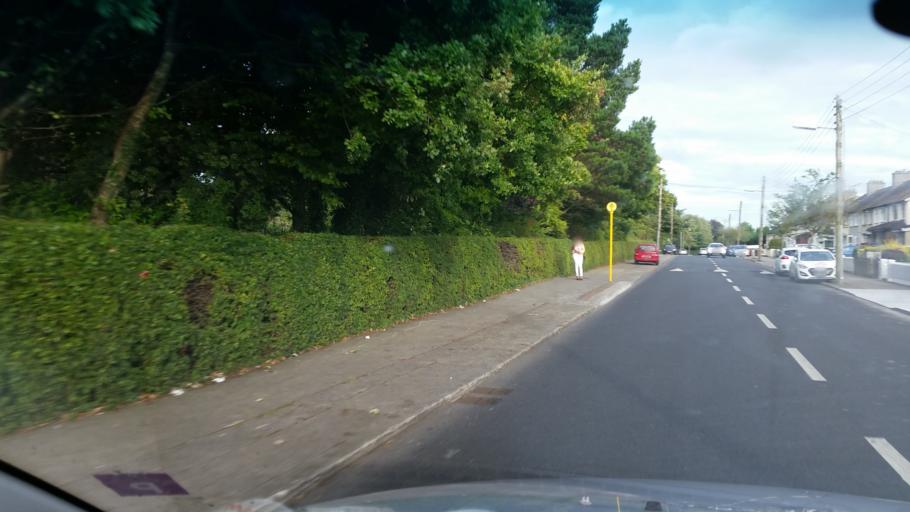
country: IE
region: Leinster
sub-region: Dublin City
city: Finglas
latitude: 53.3844
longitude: -6.2844
